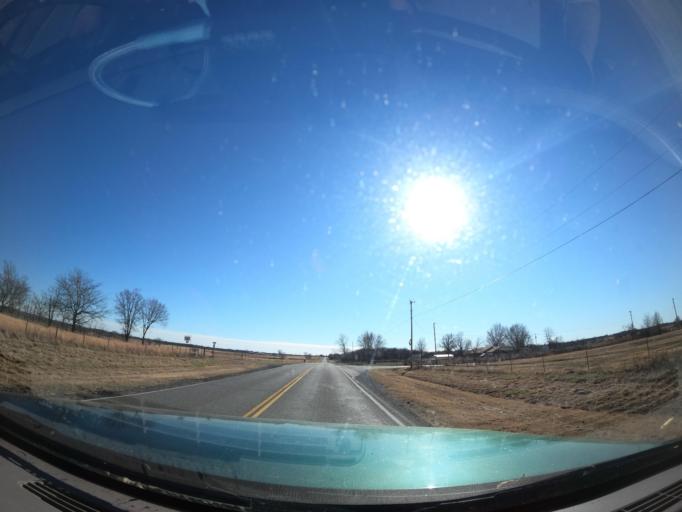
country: US
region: Oklahoma
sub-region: Muskogee County
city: Haskell
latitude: 35.6826
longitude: -95.6422
